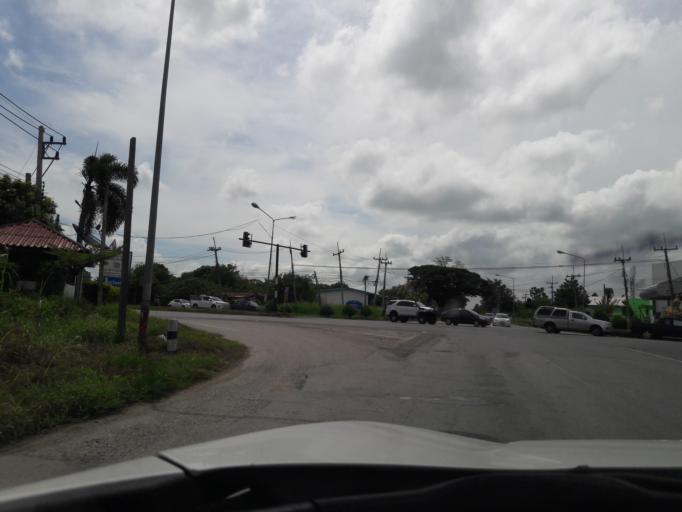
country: TH
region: Lop Buri
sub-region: Amphoe Tha Luang
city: Tha Luang
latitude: 15.0664
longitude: 101.1209
